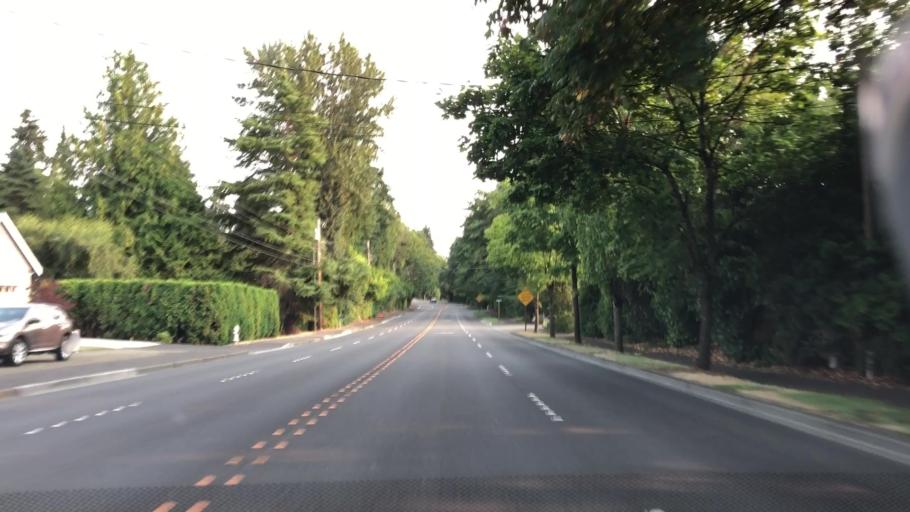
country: US
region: Washington
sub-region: King County
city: Mercer Island
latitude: 47.5701
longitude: -122.2270
